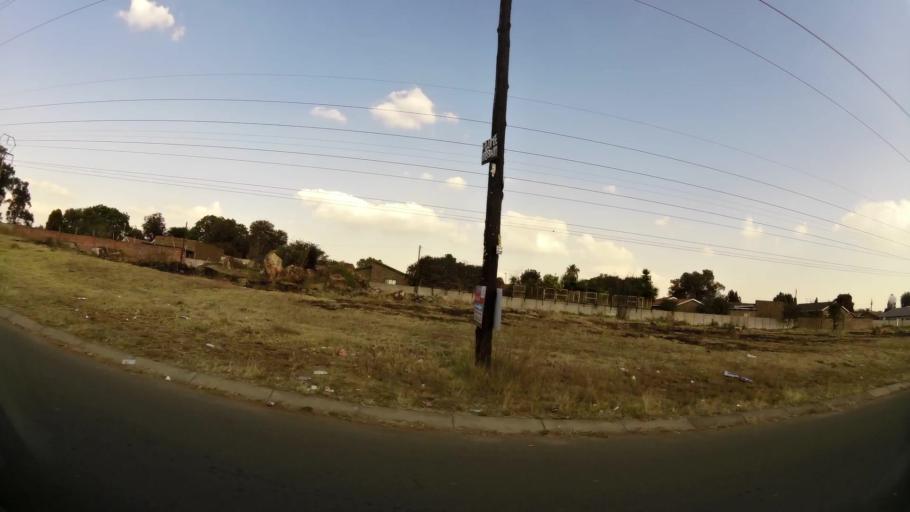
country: ZA
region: Gauteng
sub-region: Ekurhuleni Metropolitan Municipality
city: Tembisa
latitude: -25.9498
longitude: 28.2155
